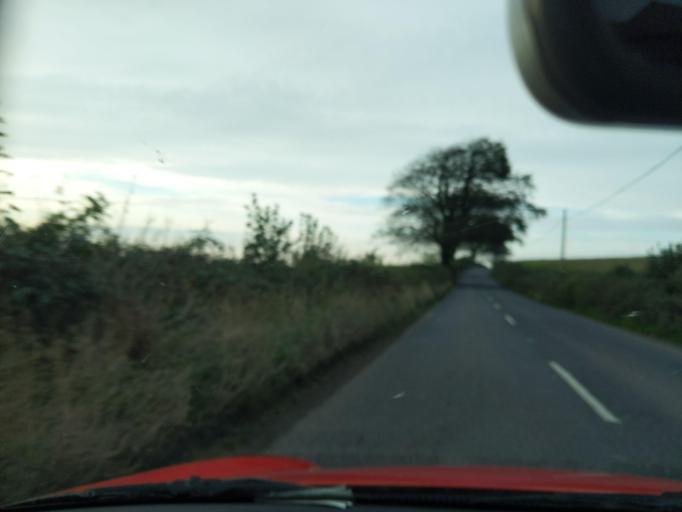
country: GB
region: England
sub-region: Devon
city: Great Torrington
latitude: 50.9235
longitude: -4.1459
